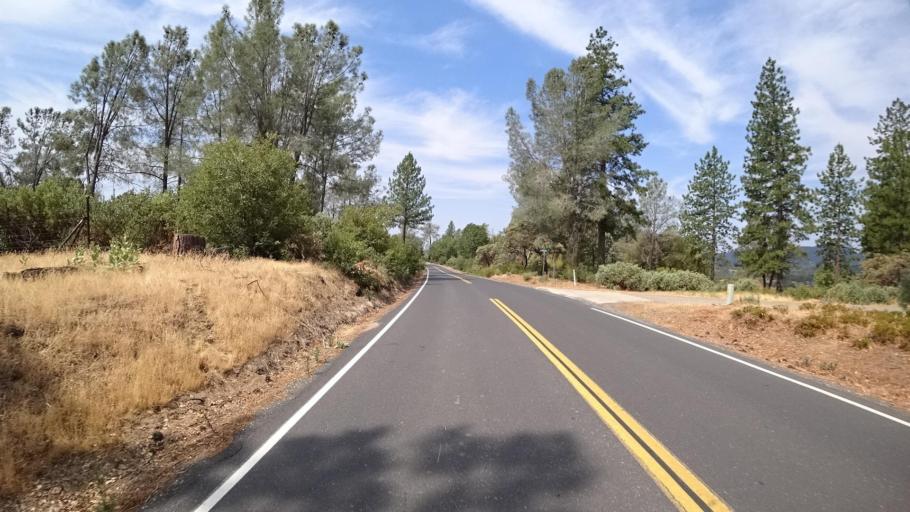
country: US
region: California
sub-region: Mariposa County
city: Midpines
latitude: 37.5018
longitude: -119.8491
